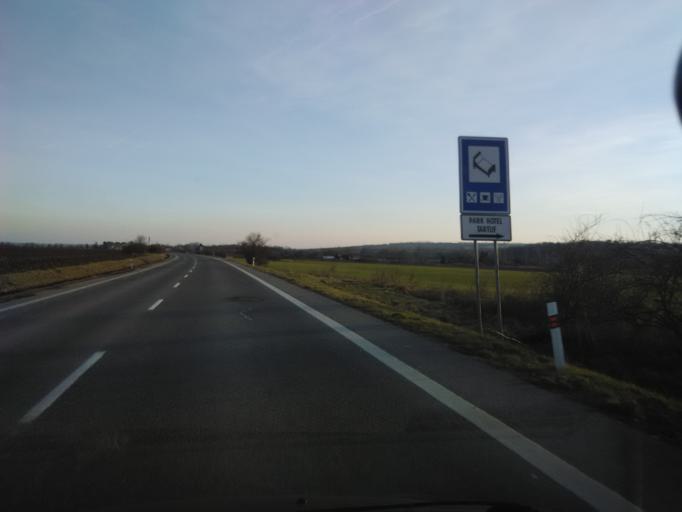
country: SK
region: Nitriansky
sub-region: Okres Nitra
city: Vrable
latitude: 48.3544
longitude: 18.2841
